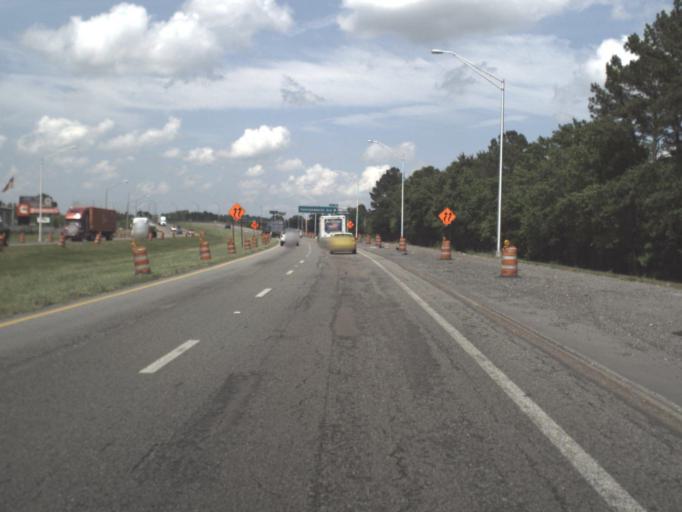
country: US
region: Florida
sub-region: Duval County
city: Jacksonville
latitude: 30.3297
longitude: -81.7644
